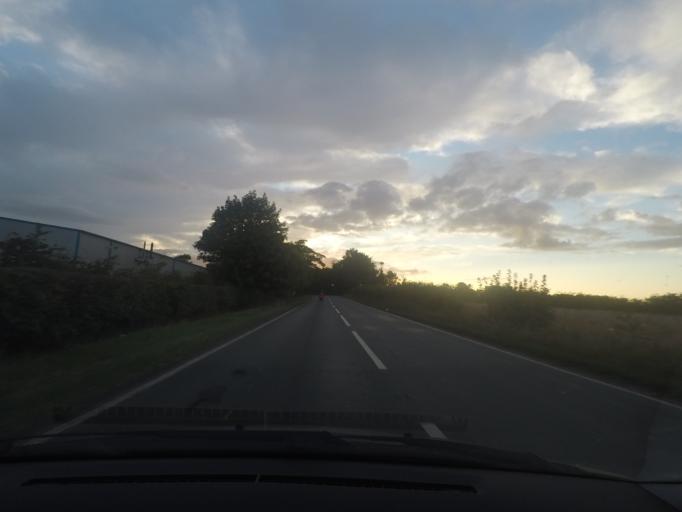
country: GB
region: England
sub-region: North Lincolnshire
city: Croxton
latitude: 53.5851
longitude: -0.3550
